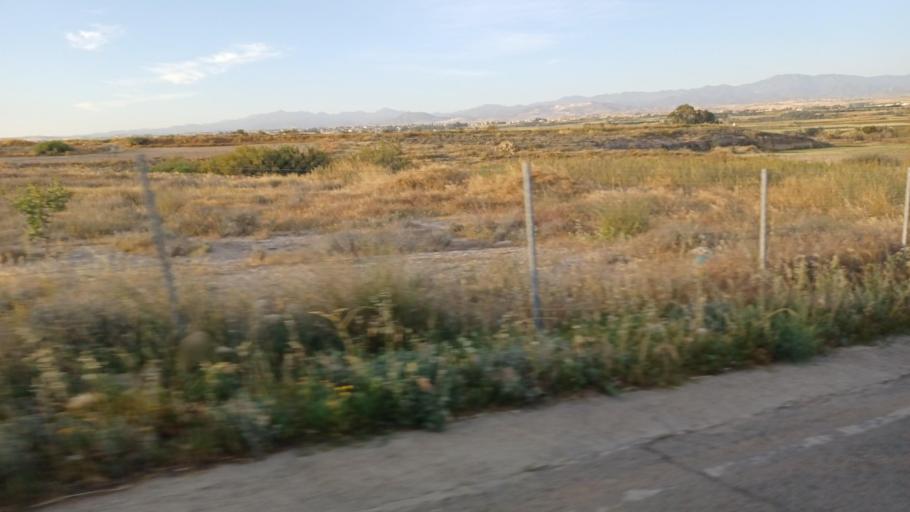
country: CY
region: Lefkosia
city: Akaki
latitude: 35.1636
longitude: 33.1405
